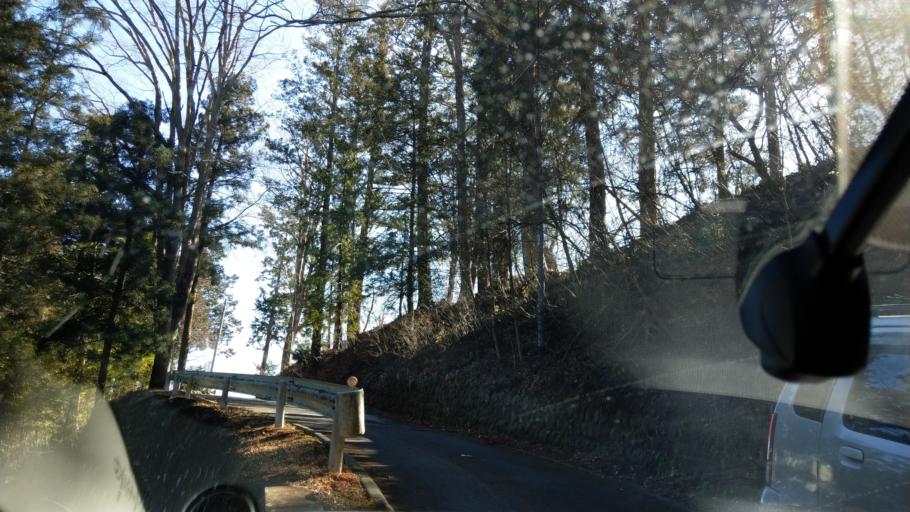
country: JP
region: Nagano
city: Saku
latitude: 36.2158
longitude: 138.4482
